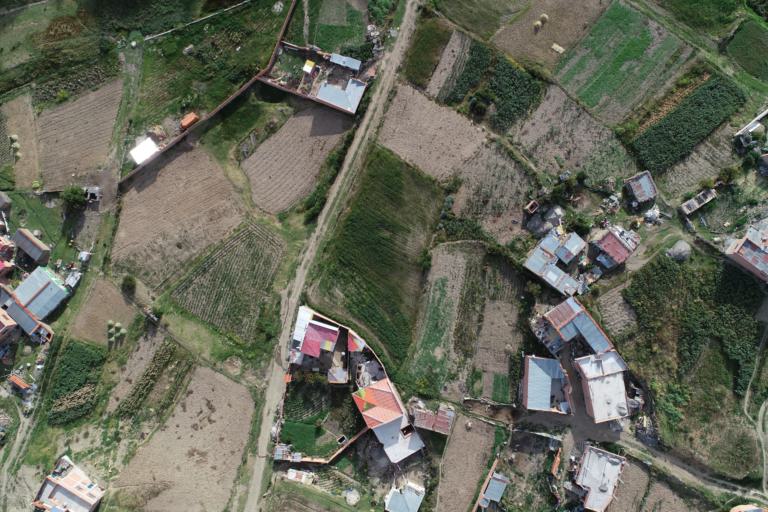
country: BO
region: La Paz
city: La Paz
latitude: -16.5450
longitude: -68.0014
